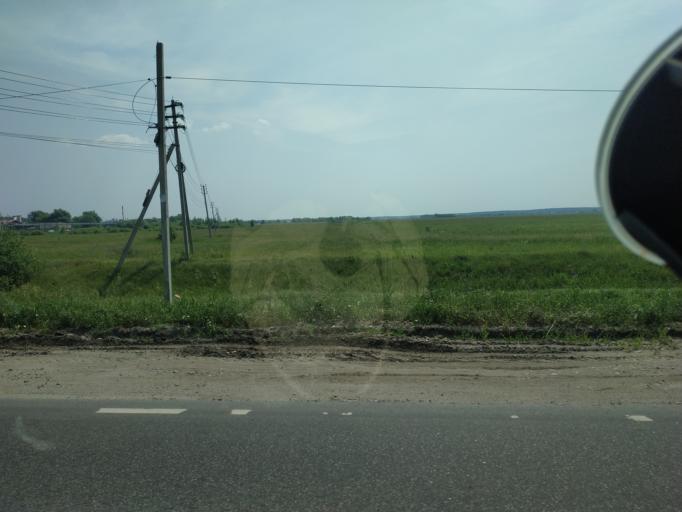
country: RU
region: Moskovskaya
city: Malyshevo
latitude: 55.5075
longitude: 38.2968
